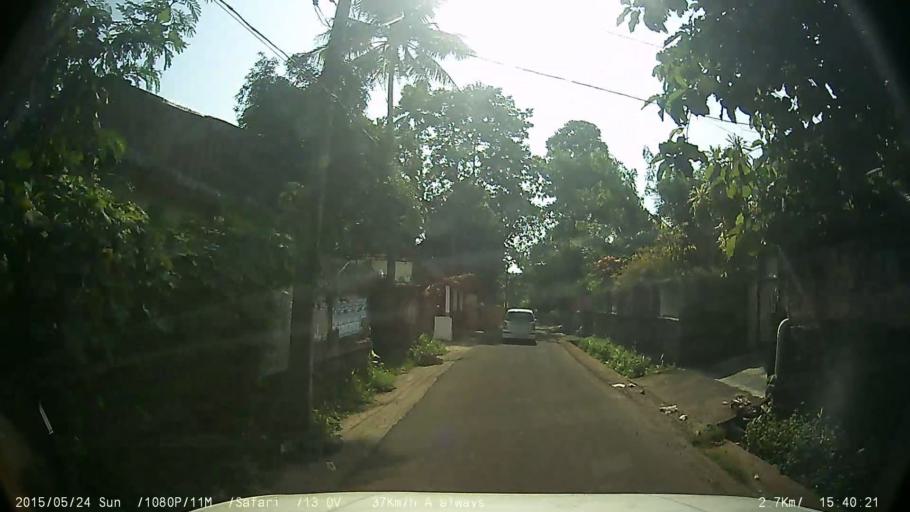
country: IN
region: Kerala
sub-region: Kottayam
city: Changanacheri
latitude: 9.4409
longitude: 76.5478
